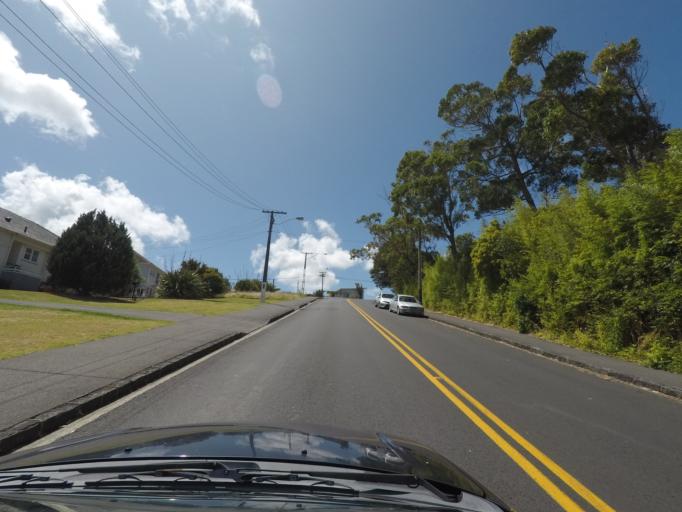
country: NZ
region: Auckland
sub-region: Auckland
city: Auckland
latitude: -36.8604
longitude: 174.7212
